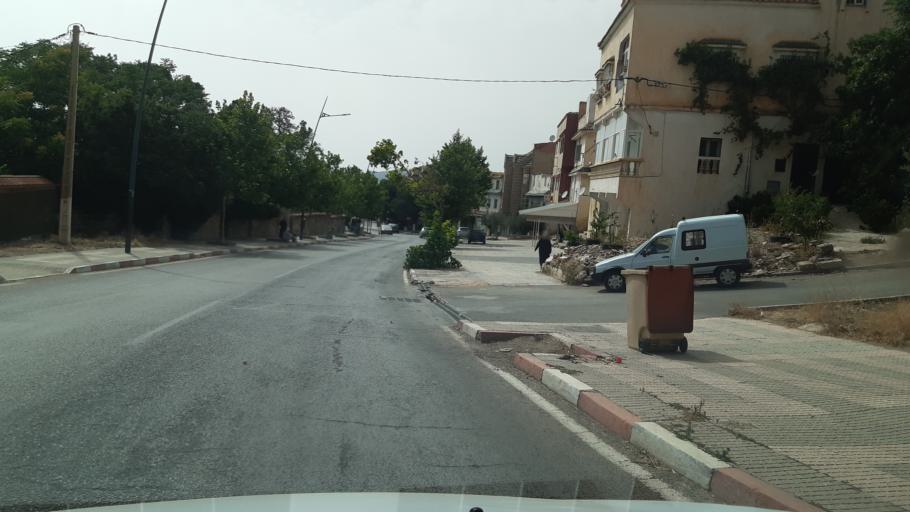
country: MA
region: Meknes-Tafilalet
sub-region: Ifrane
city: Azrou
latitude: 33.4371
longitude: -5.2198
